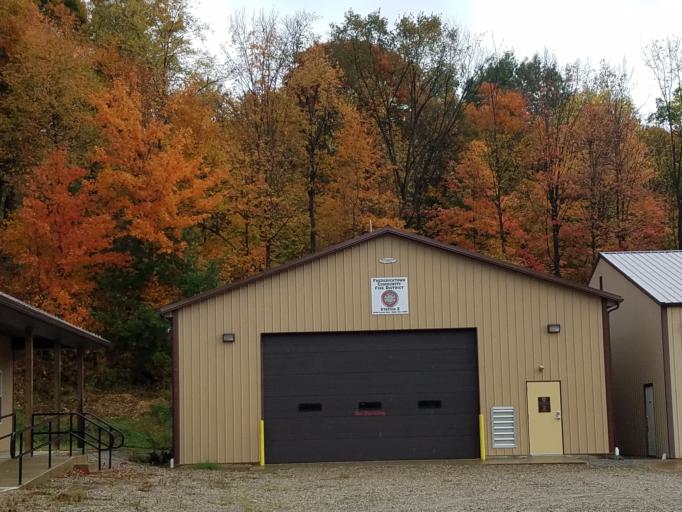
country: US
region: Ohio
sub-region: Knox County
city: Fredericktown
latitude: 40.5090
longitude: -82.4125
